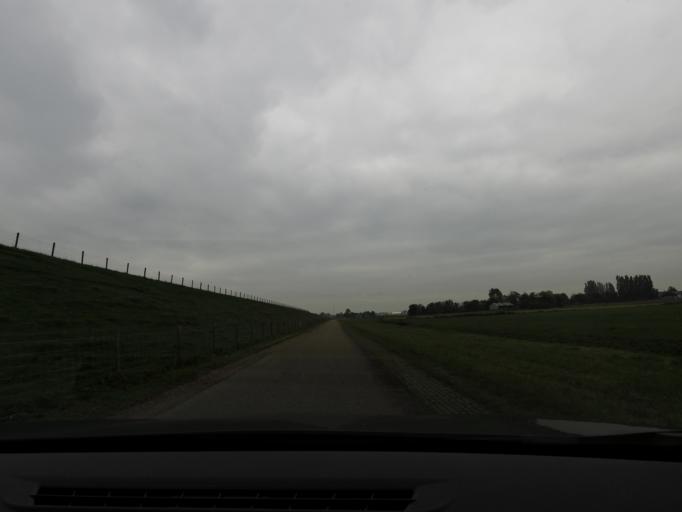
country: NL
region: South Holland
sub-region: Gemeente Hellevoetsluis
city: Hellevoetsluis
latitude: 51.8122
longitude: 4.1731
